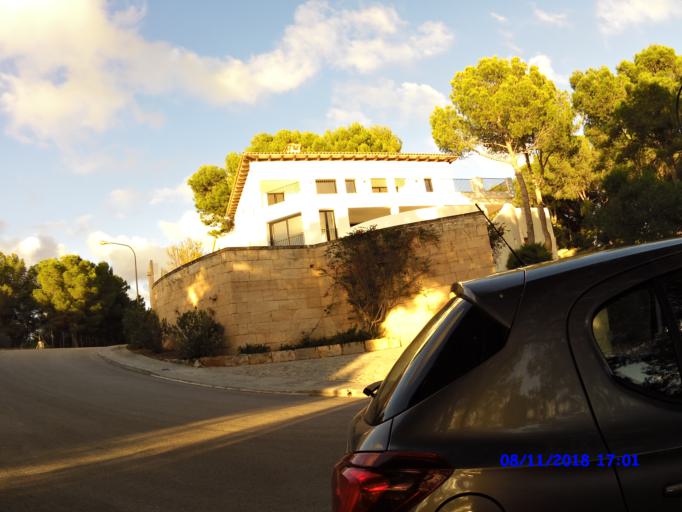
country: ES
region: Balearic Islands
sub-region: Illes Balears
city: Santa Ponsa
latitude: 39.5333
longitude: 2.4615
